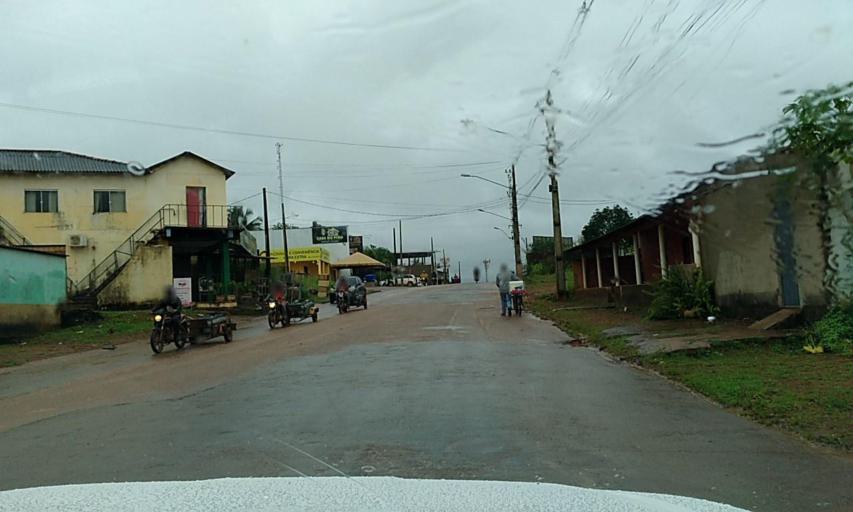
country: BR
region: Para
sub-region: Altamira
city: Altamira
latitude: -3.2134
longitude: -52.2341
